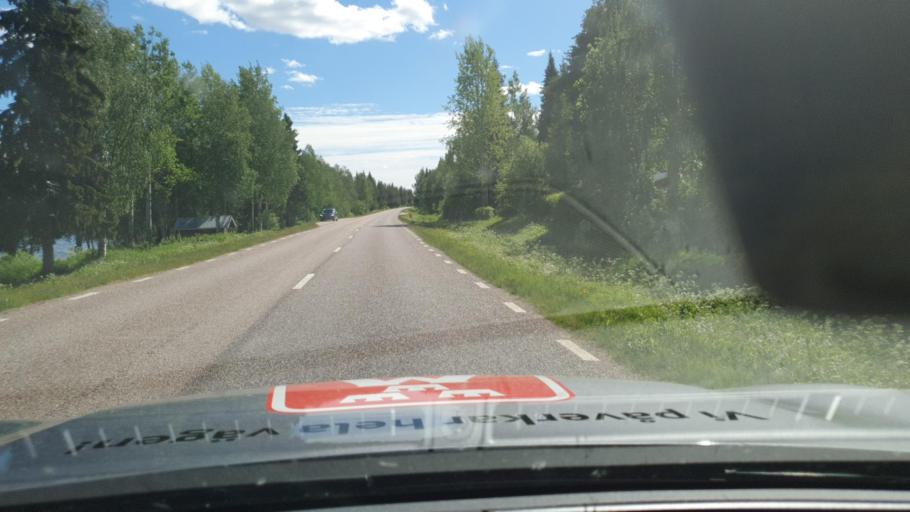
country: FI
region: Lapland
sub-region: Tunturi-Lappi
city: Kolari
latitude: 67.0636
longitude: 23.6697
